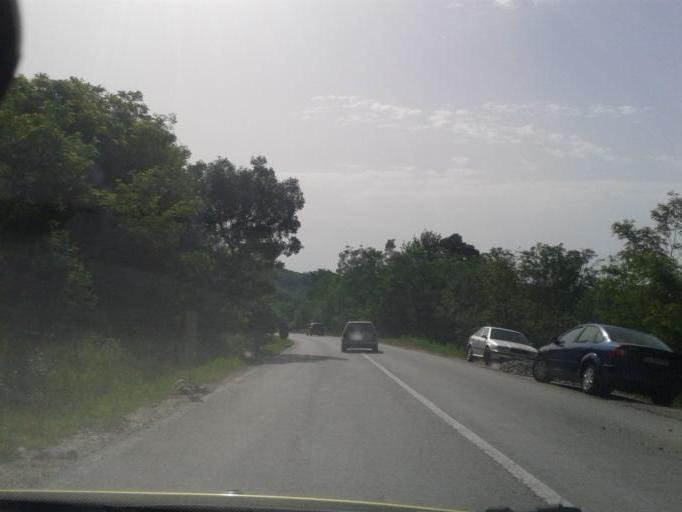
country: RO
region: Valcea
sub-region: Comuna Costesti
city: Costesti
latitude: 45.1413
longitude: 24.0780
